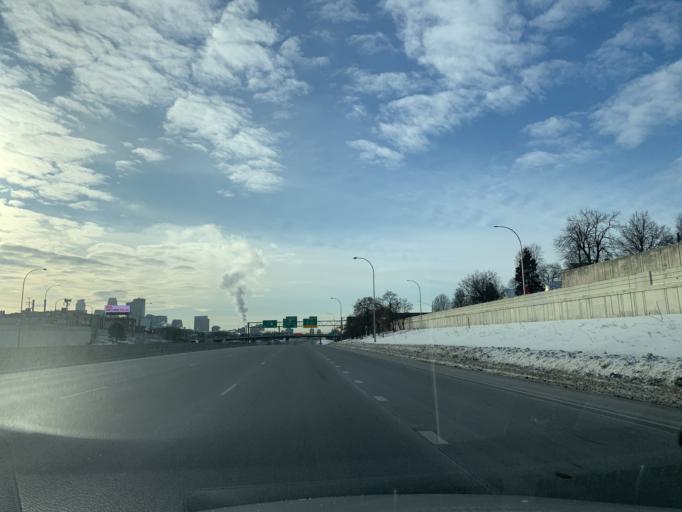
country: US
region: Minnesota
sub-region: Hennepin County
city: Minneapolis
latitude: 45.0032
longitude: -93.2829
